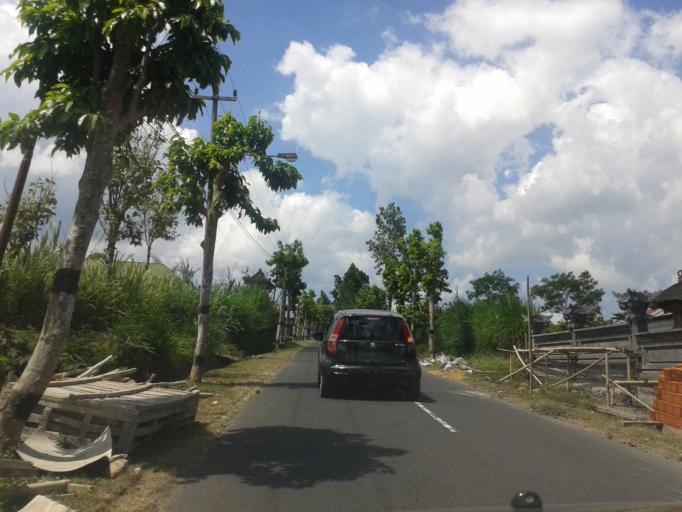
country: ID
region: Bali
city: Banjar Kedisan
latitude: -8.3186
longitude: 115.3303
